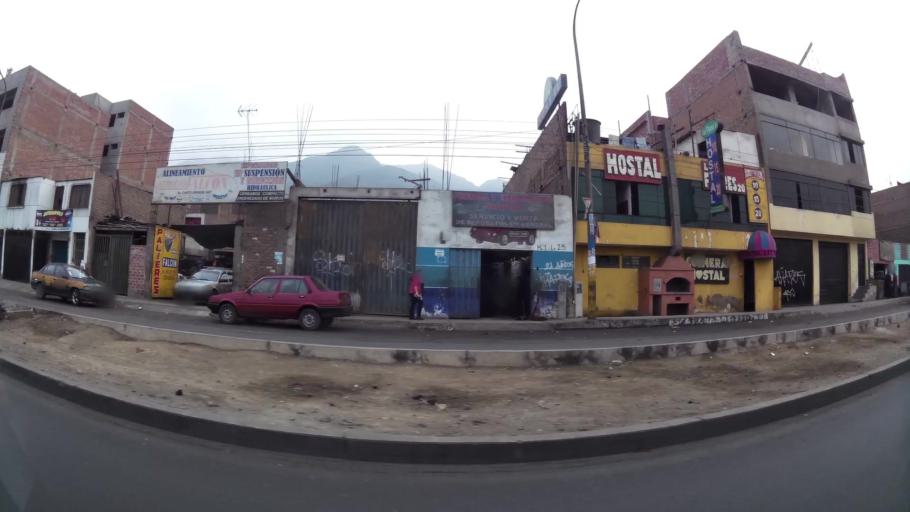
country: PE
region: Lima
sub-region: Lima
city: Independencia
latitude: -11.9881
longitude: -77.0157
